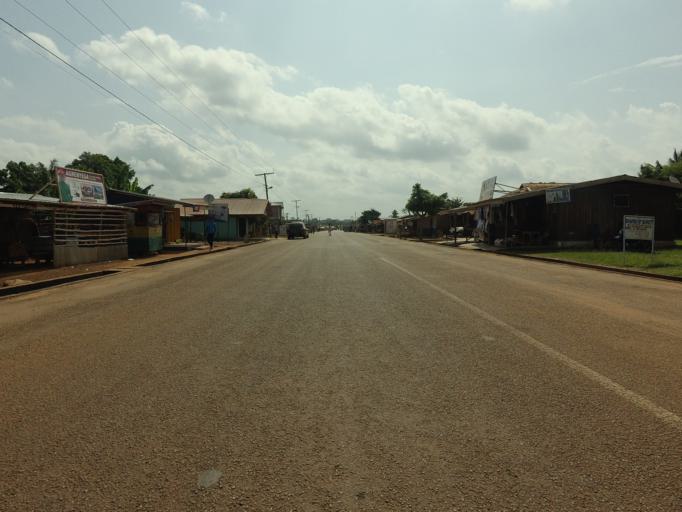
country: TG
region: Maritime
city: Tsevie
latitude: 6.3619
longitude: 0.8590
